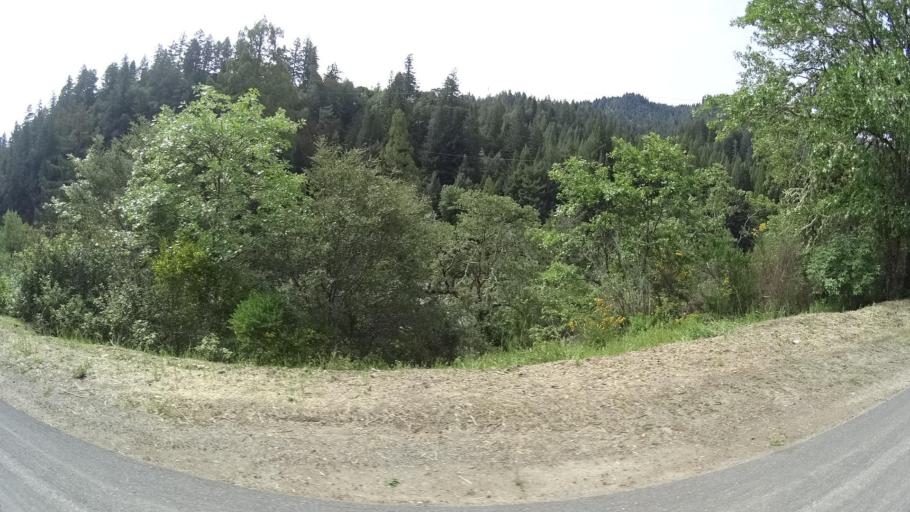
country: US
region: California
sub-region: Humboldt County
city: Redway
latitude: 40.1151
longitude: -123.8125
